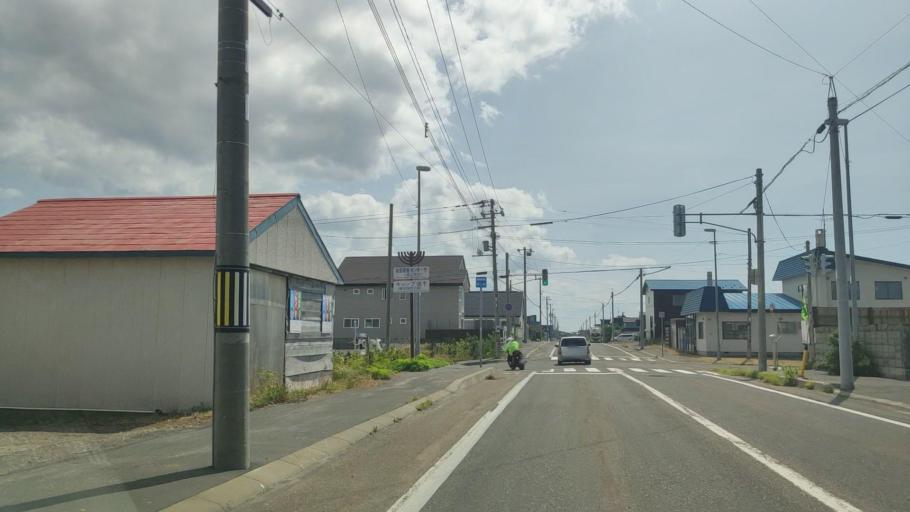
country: JP
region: Hokkaido
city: Makubetsu
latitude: 44.8831
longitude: 141.7430
